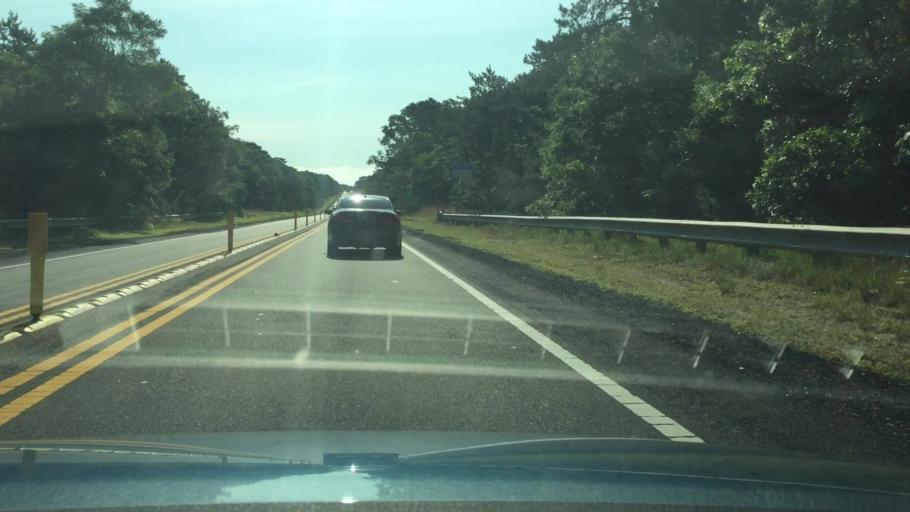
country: US
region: Massachusetts
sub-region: Barnstable County
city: South Dennis
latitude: 41.7004
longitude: -70.1315
